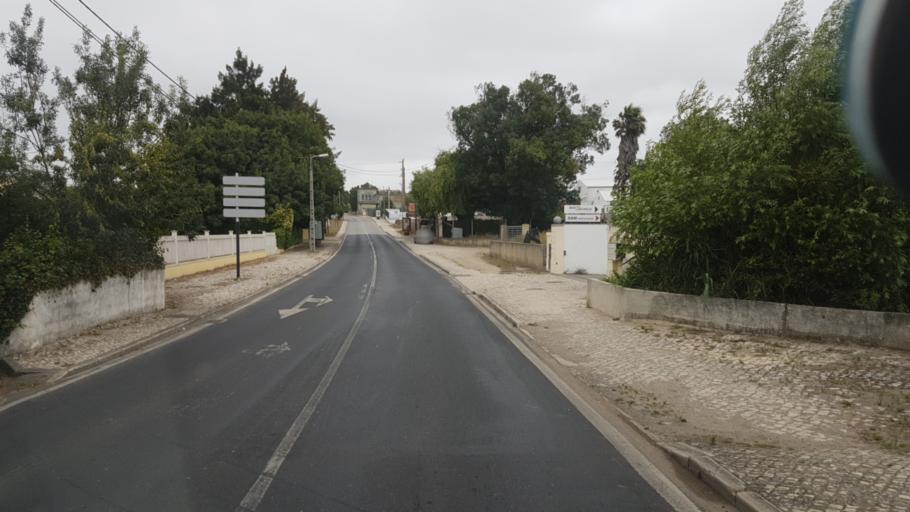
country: PT
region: Lisbon
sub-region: Sintra
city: Pero Pinheiro
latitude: 38.8490
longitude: -9.3272
